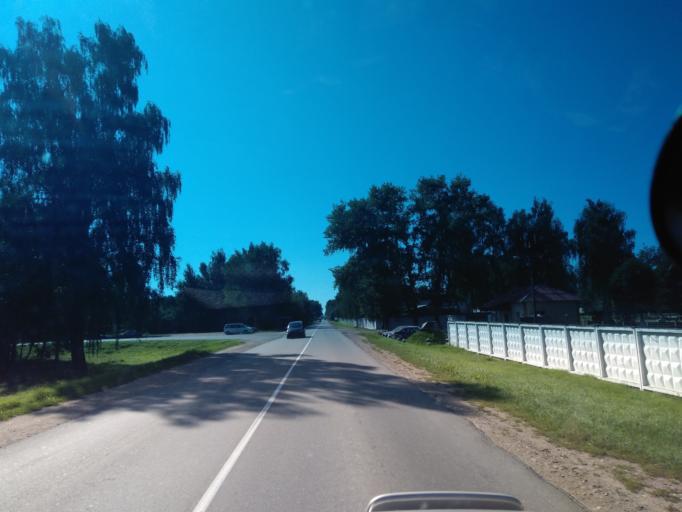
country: BY
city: Fanipol
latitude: 53.7112
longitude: 27.3463
